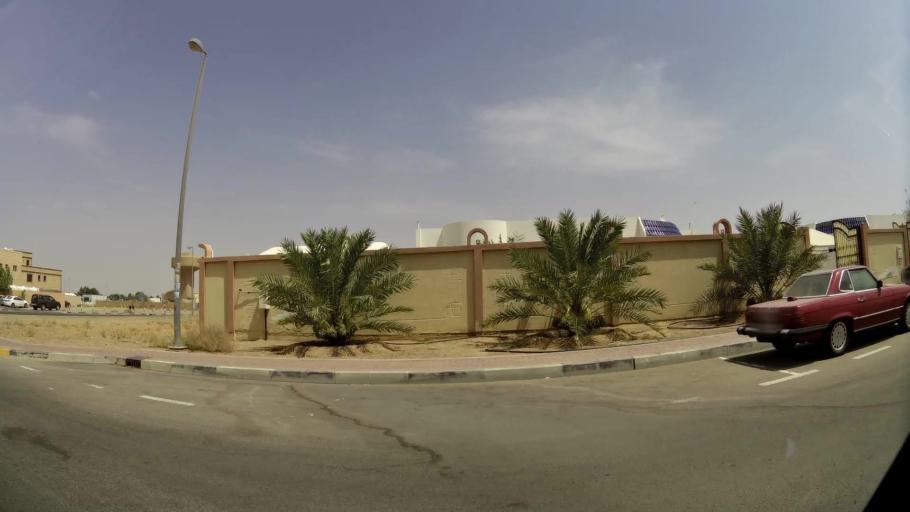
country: AE
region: Abu Dhabi
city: Al Ain
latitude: 24.1712
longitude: 55.7129
